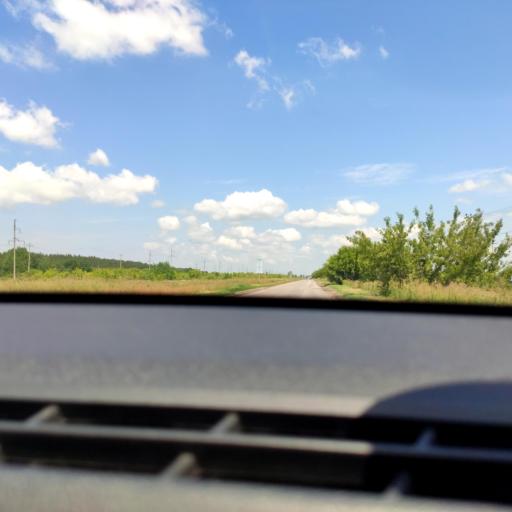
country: RU
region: Samara
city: Podstepki
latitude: 53.5331
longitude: 49.0856
